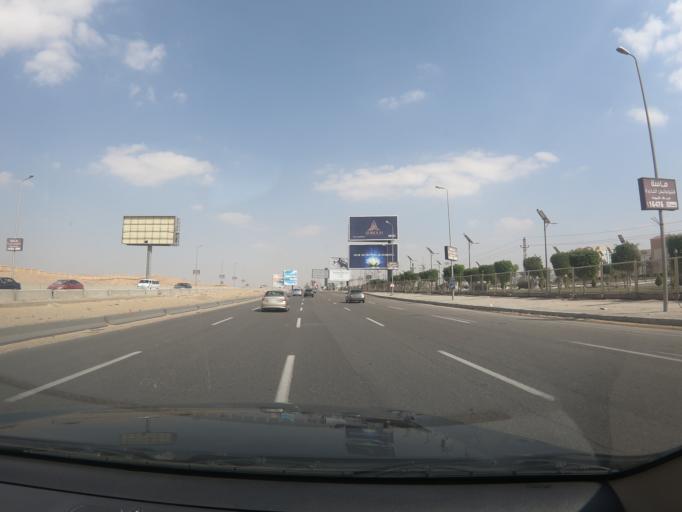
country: EG
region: Muhafazat al Qalyubiyah
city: Al Khankah
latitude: 30.0850
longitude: 31.5006
